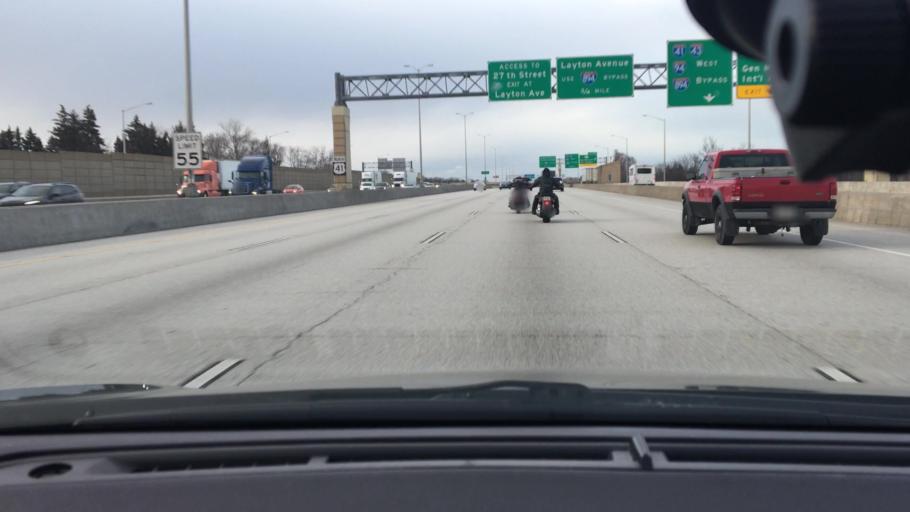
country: US
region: Wisconsin
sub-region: Milwaukee County
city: Greendale
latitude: 42.9345
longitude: -87.9350
